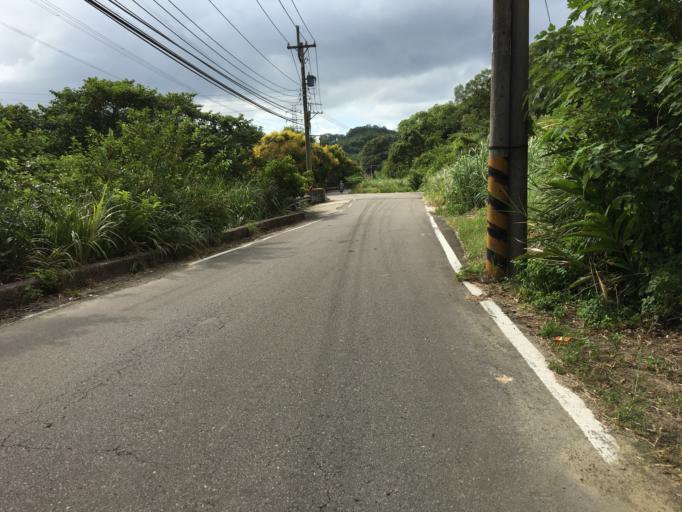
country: TW
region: Taiwan
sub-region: Hsinchu
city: Hsinchu
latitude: 24.7007
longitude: 120.9600
